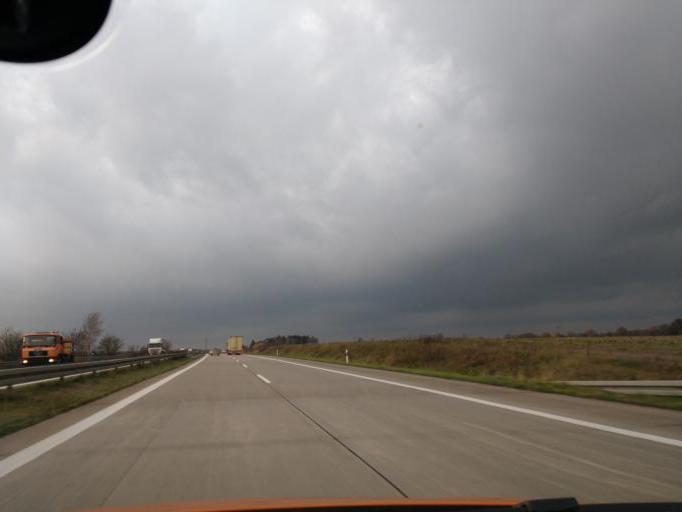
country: DE
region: Brandenburg
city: Heiligengrabe
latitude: 53.1660
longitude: 12.3743
